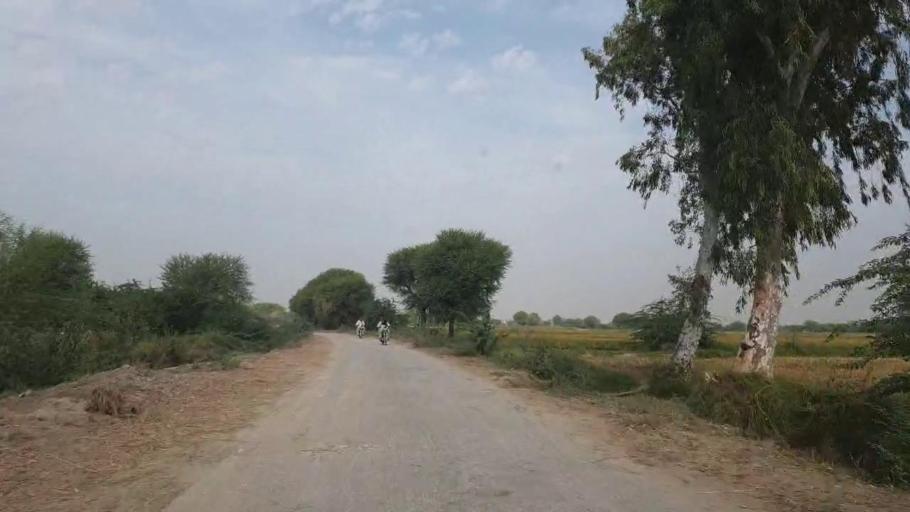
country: PK
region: Sindh
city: Rajo Khanani
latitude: 24.9444
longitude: 68.9812
